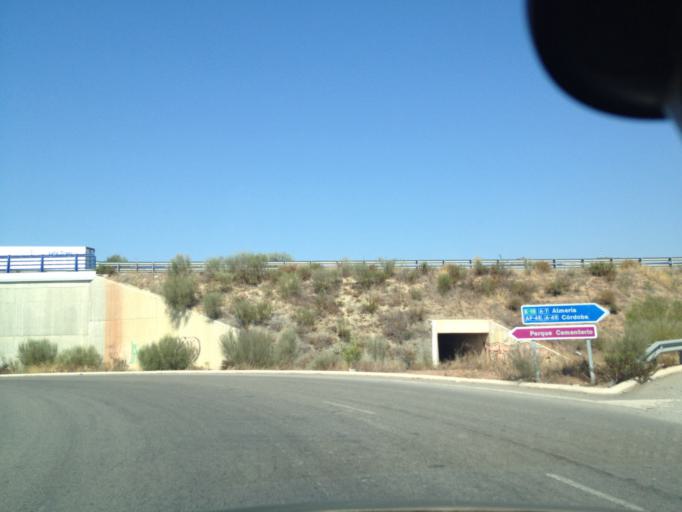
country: ES
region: Andalusia
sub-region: Provincia de Malaga
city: Alhaurin de la Torre
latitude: 36.7192
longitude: -4.5124
